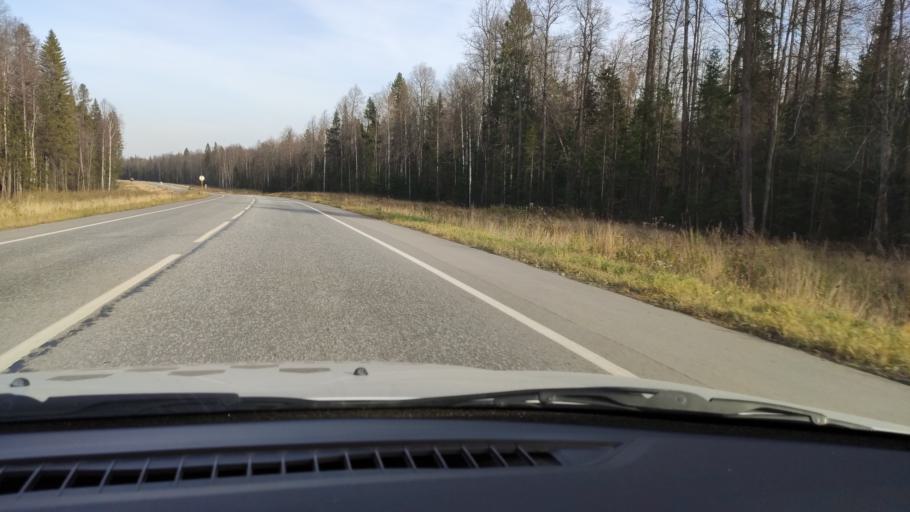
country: RU
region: Perm
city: Novyye Lyady
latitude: 58.0365
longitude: 56.5353
